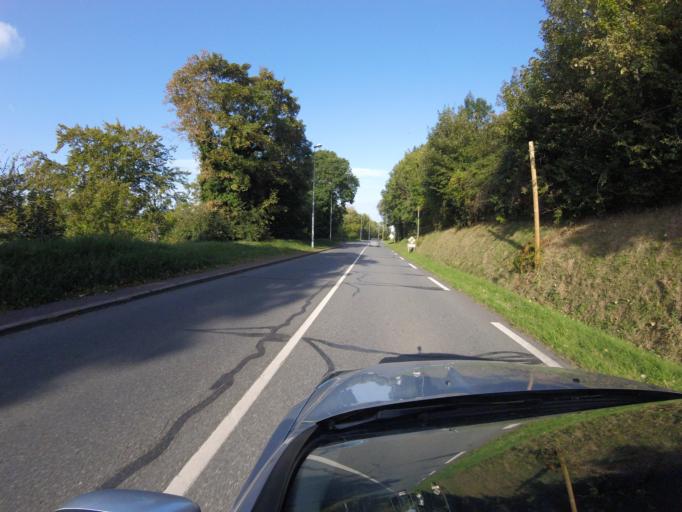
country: FR
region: Haute-Normandie
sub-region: Departement de la Seine-Maritime
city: Fecamp
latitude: 49.7595
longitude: 0.3897
